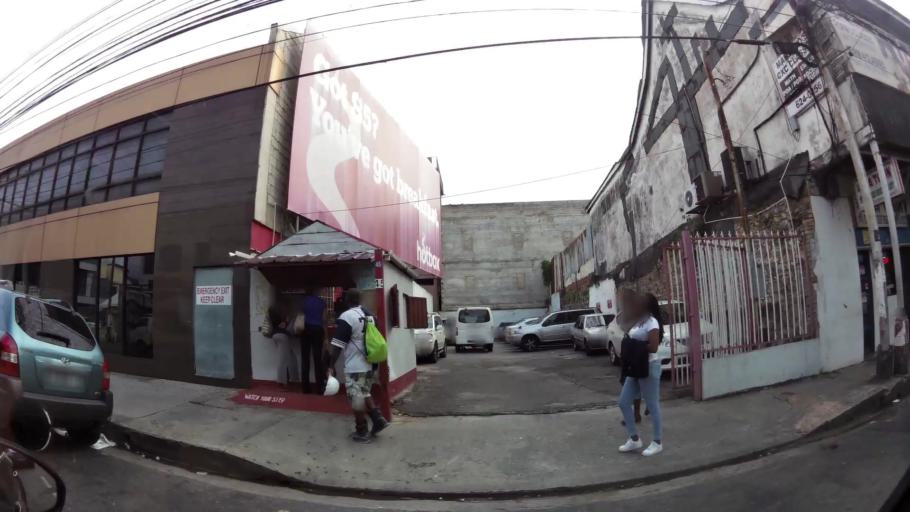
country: TT
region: City of Port of Spain
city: Port-of-Spain
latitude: 10.6566
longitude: -61.5111
